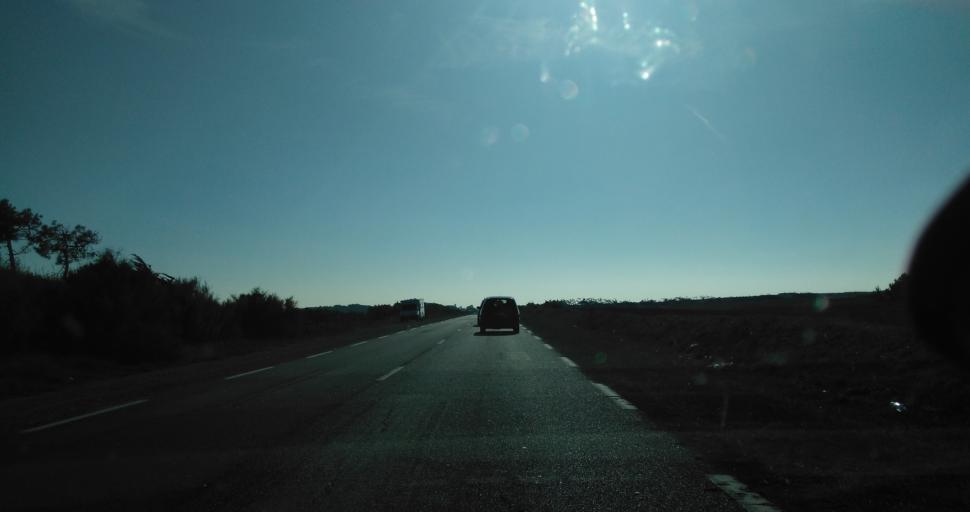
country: FR
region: Brittany
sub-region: Departement du Morbihan
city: Plouharnel
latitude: 47.5853
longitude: -3.1340
